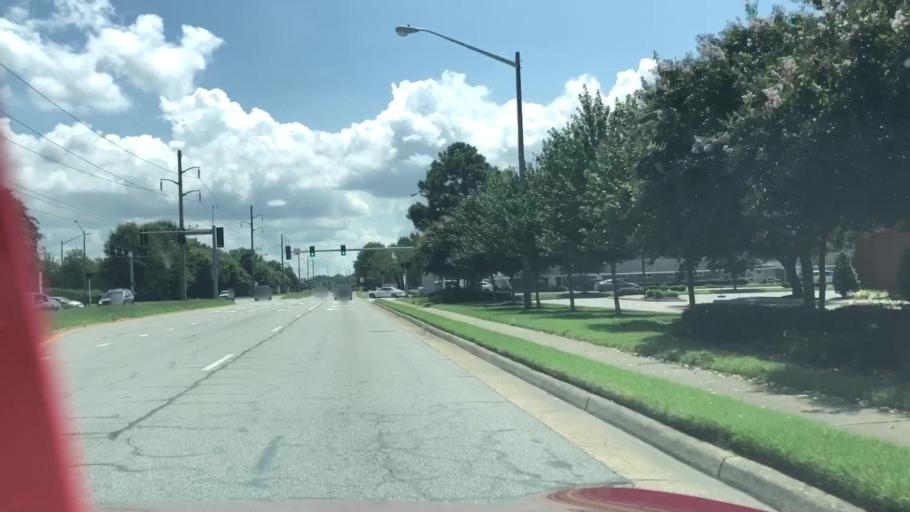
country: US
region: Virginia
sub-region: City of Virginia Beach
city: Virginia Beach
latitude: 36.8663
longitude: -76.0295
